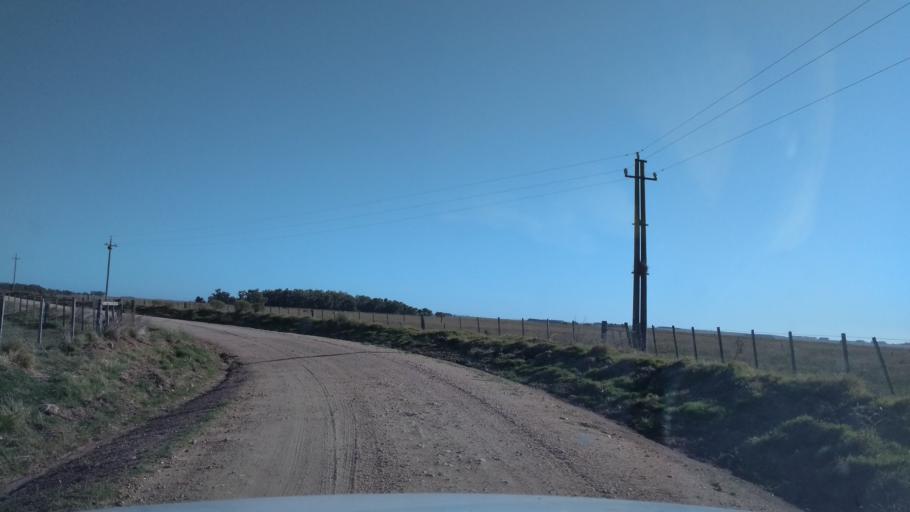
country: UY
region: Florida
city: Casupa
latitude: -34.0353
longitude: -55.7799
